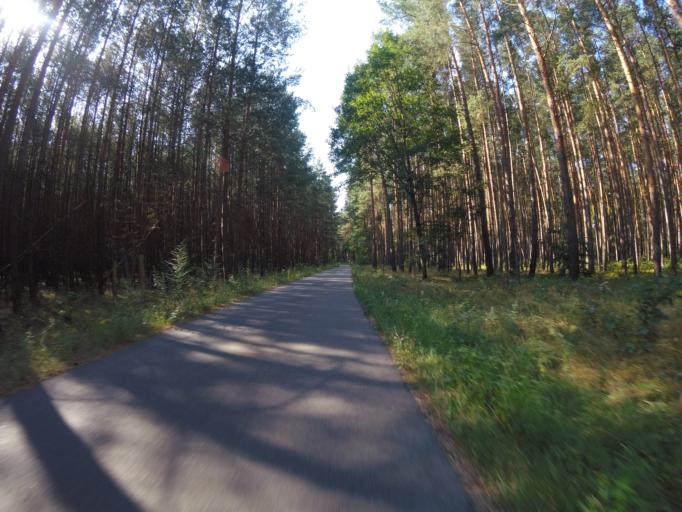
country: DE
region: Brandenburg
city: Berkenbruck
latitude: 52.3136
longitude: 14.2118
